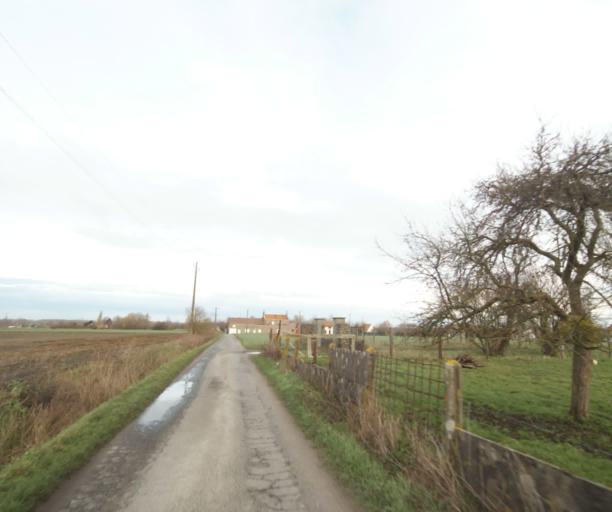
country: BE
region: Wallonia
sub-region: Province du Hainaut
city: Peruwelz
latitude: 50.4922
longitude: 3.5773
